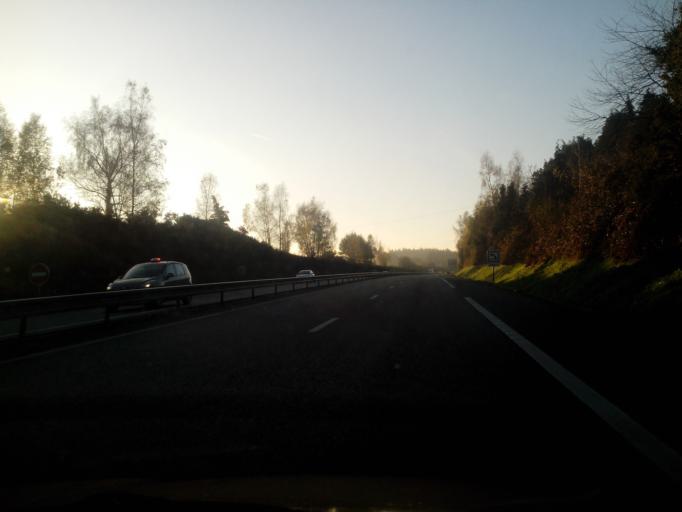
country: FR
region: Brittany
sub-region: Departement du Morbihan
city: Guillac
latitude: 47.8689
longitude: -2.4180
